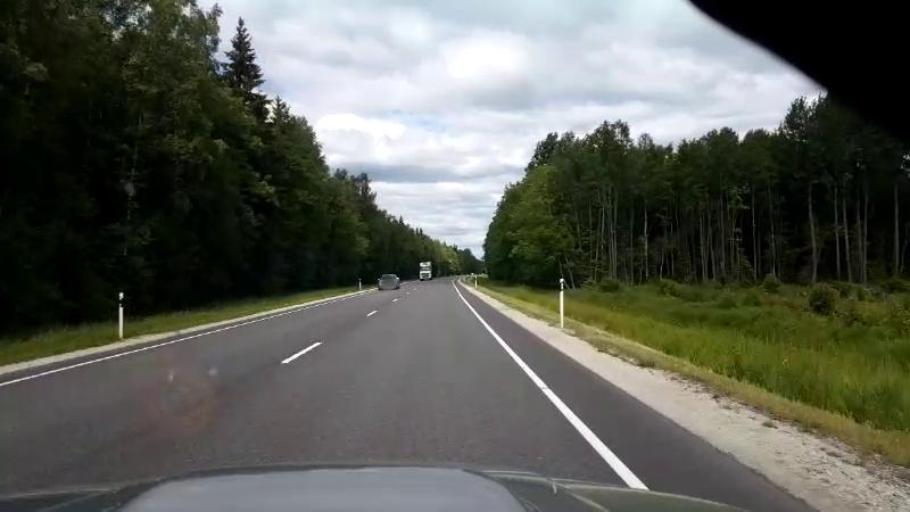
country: EE
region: Raplamaa
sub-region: Maerjamaa vald
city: Marjamaa
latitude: 58.8257
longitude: 24.4151
